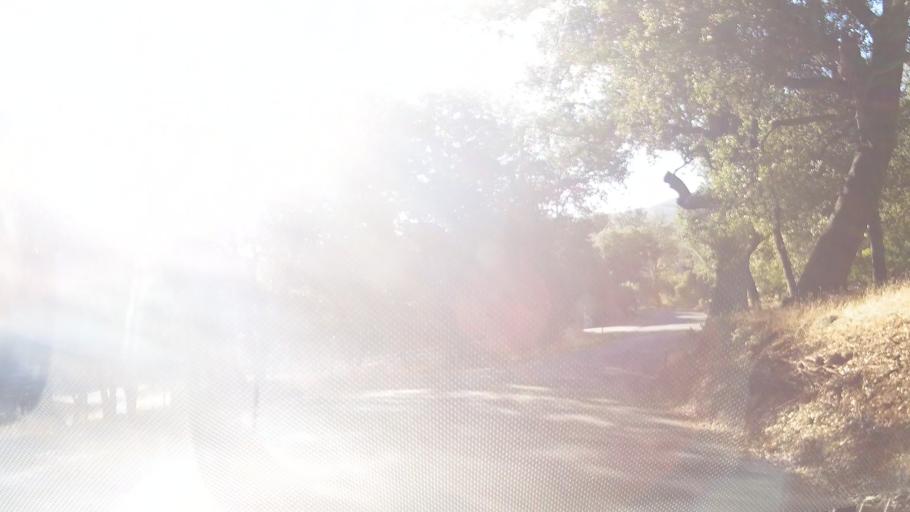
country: US
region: California
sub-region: San Diego County
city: Julian
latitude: 33.0468
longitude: -116.6221
